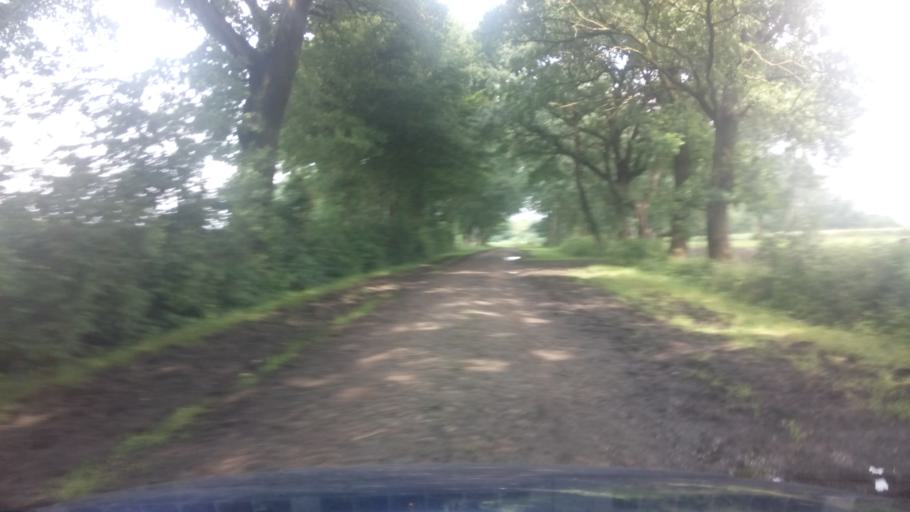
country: DE
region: Lower Saxony
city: Osterholz-Scharmbeck
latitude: 53.2359
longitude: 8.7474
